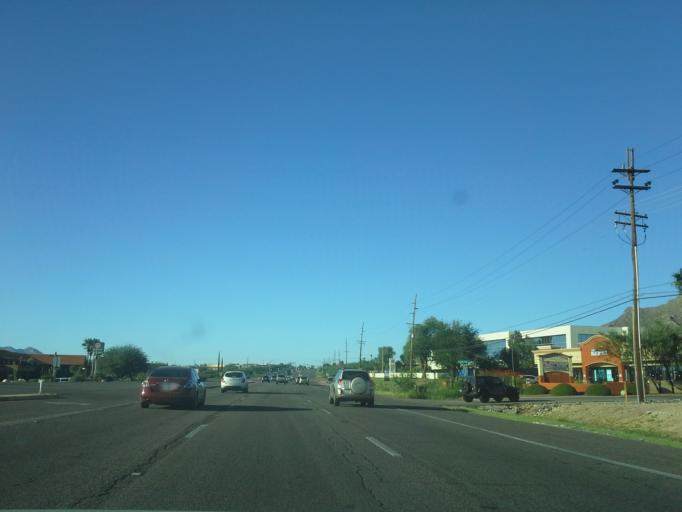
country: US
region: Arizona
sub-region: Pima County
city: Casas Adobes
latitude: 32.3398
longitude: -110.9772
